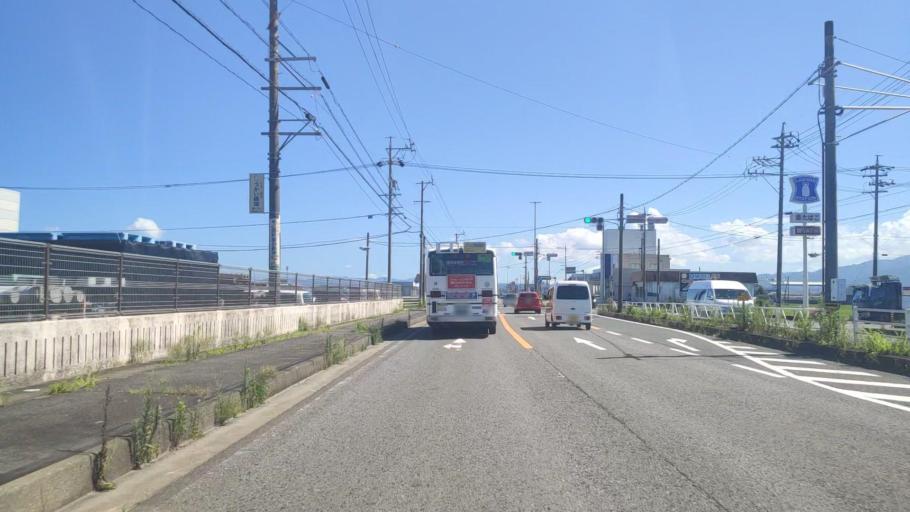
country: JP
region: Mie
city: Hisai-motomachi
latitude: 34.6410
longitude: 136.5183
